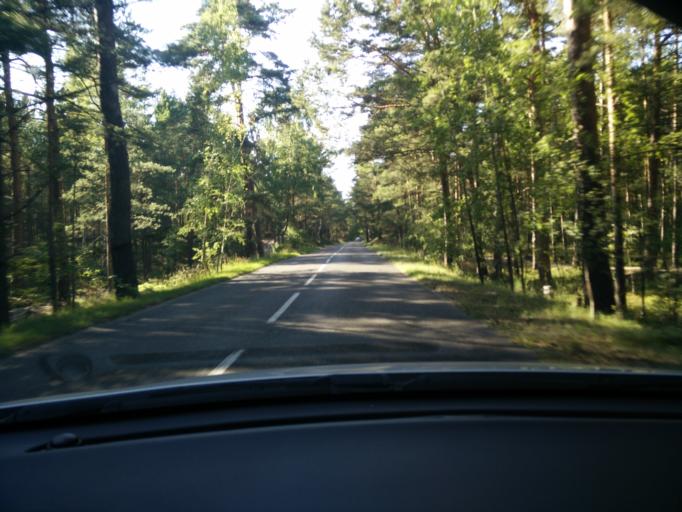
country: PL
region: Pomeranian Voivodeship
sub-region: Powiat pucki
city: Hel
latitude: 54.6307
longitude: 18.7870
